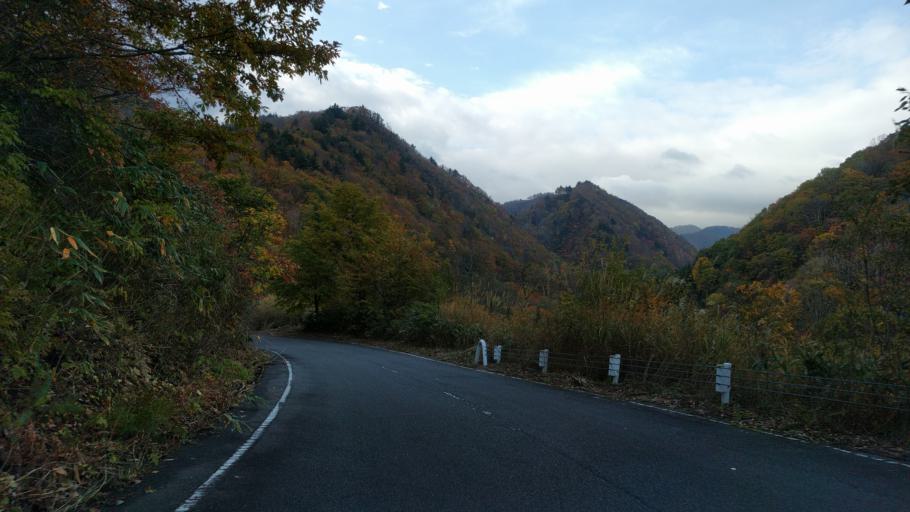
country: JP
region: Fukushima
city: Kitakata
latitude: 37.4011
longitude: 139.7604
